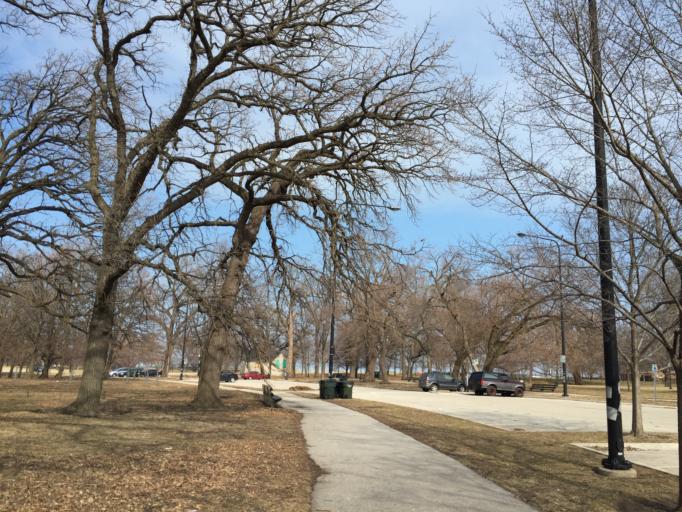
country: US
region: Illinois
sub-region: Cook County
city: Chicago
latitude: 41.7888
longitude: -87.5813
